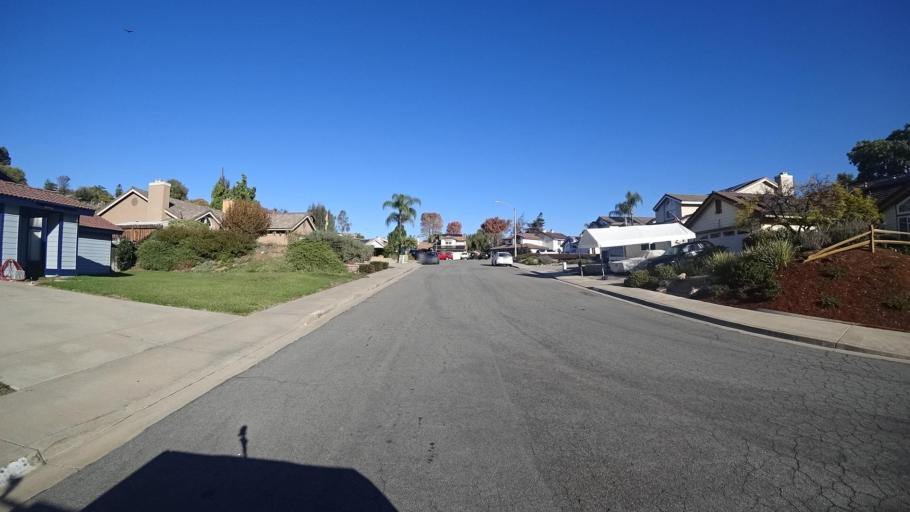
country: US
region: California
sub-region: San Diego County
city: Winter Gardens
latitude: 32.8350
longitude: -116.9133
